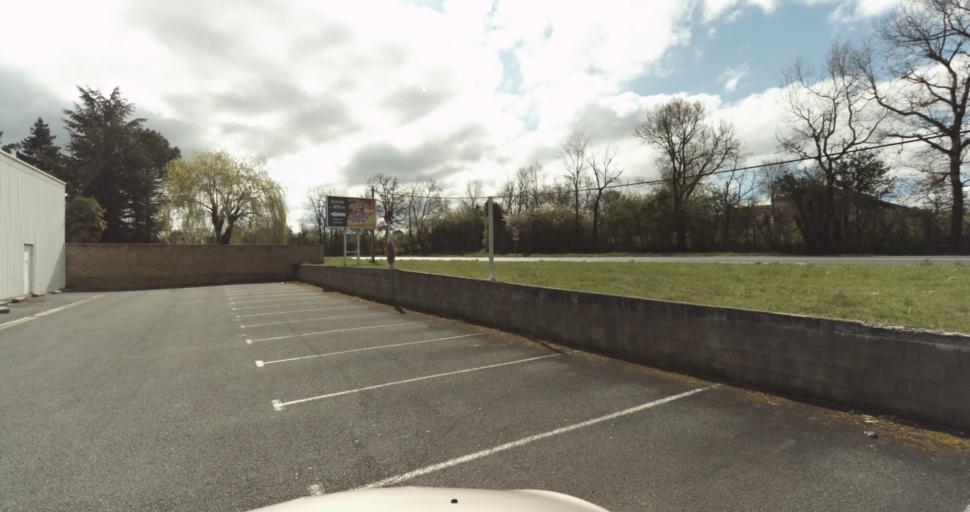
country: FR
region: Midi-Pyrenees
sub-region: Departement du Tarn
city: Puygouzon
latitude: 43.8920
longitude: 2.1569
